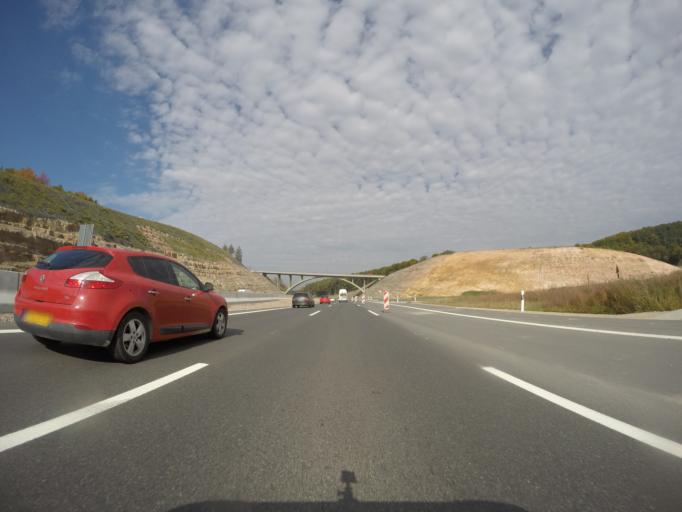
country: DE
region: Bavaria
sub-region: Regierungsbezirk Unterfranken
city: Weibersbrunn
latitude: 49.9388
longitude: 9.3452
